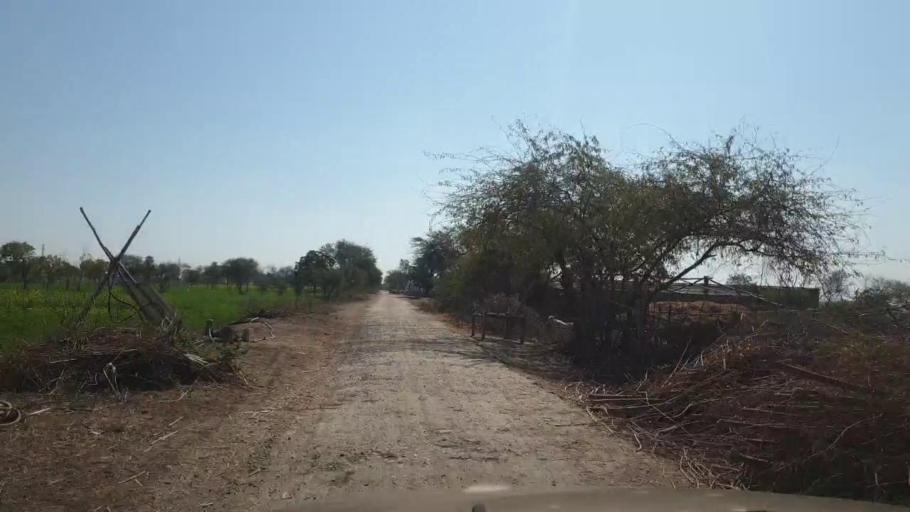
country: PK
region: Sindh
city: Mirpur Khas
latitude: 25.5575
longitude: 69.0653
